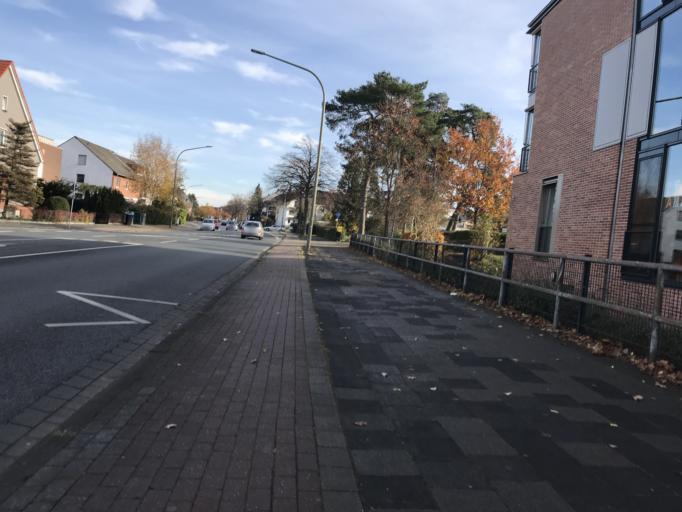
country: DE
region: North Rhine-Westphalia
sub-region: Regierungsbezirk Arnsberg
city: Hamm
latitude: 51.6910
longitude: 7.8620
